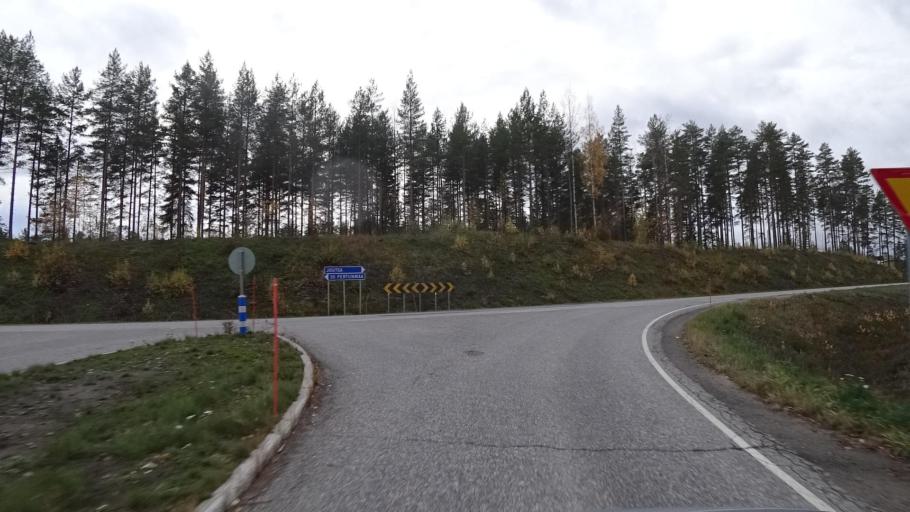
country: FI
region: Central Finland
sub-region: Joutsa
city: Joutsa
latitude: 61.7492
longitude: 26.1338
